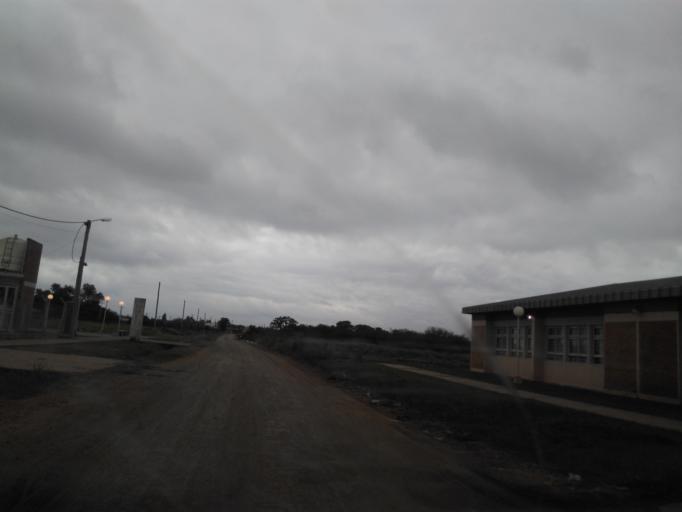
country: AR
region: Chaco
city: Fontana
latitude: -27.4555
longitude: -59.0445
